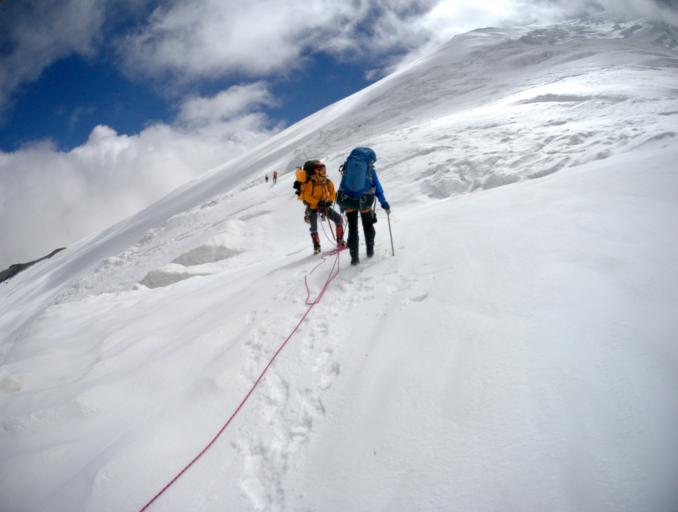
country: RU
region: Kabardino-Balkariya
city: Terskol
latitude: 43.3800
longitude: 42.4528
